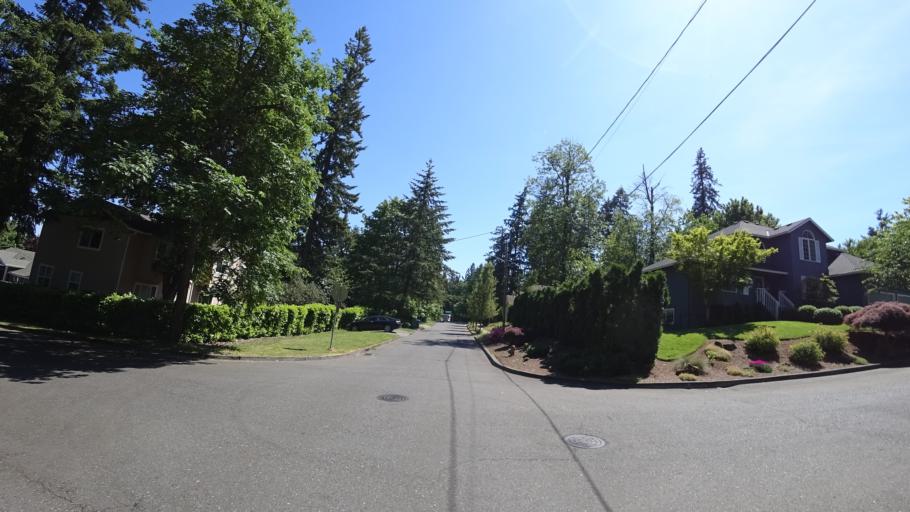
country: US
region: Oregon
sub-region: Washington County
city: Metzger
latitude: 45.4462
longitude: -122.7151
